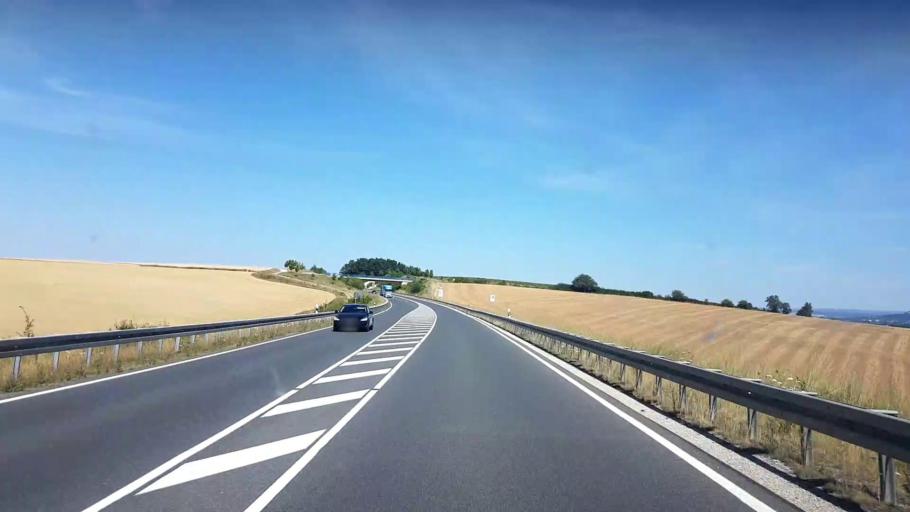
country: DE
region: Bavaria
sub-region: Upper Franconia
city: Untersiemau
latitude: 50.1753
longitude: 10.9865
